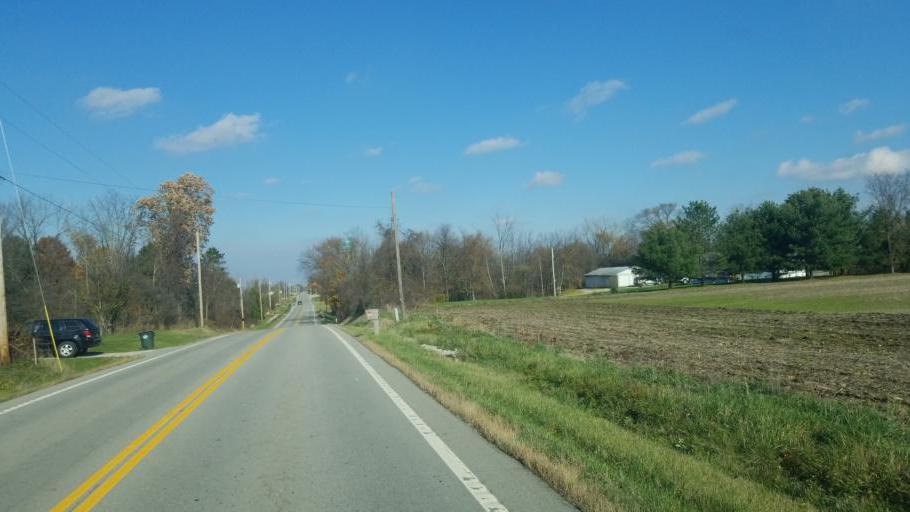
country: US
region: Ohio
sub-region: Huron County
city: New London
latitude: 41.0824
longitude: -82.3040
